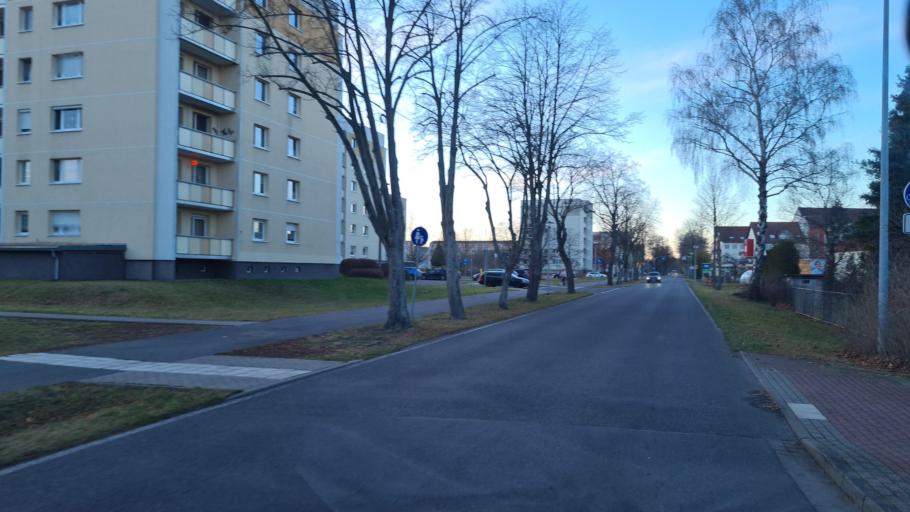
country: DE
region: Brandenburg
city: Vetschau
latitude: 51.7785
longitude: 14.0861
